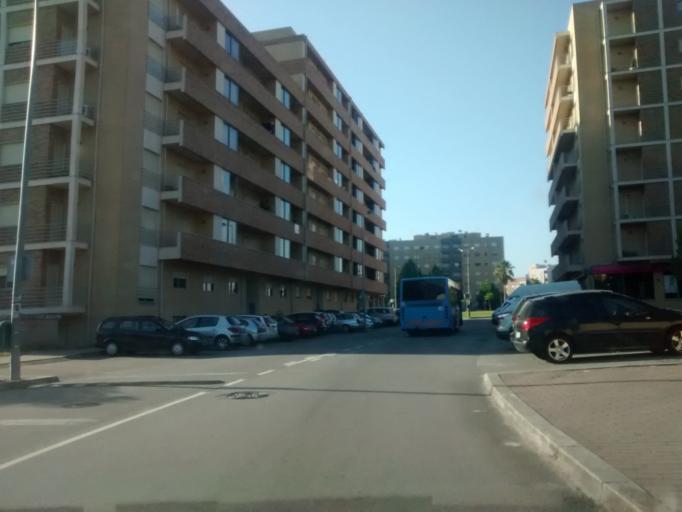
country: PT
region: Braga
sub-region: Braga
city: Braga
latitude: 41.5471
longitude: -8.4031
